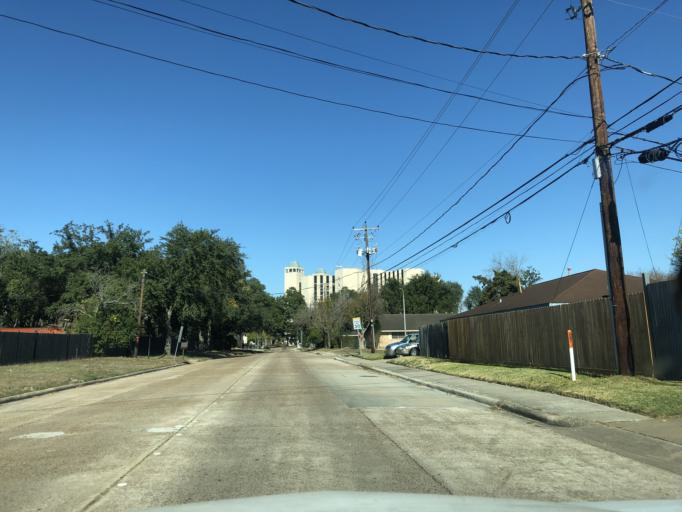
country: US
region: Texas
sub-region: Harris County
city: Bellaire
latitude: 29.6893
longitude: -95.5219
